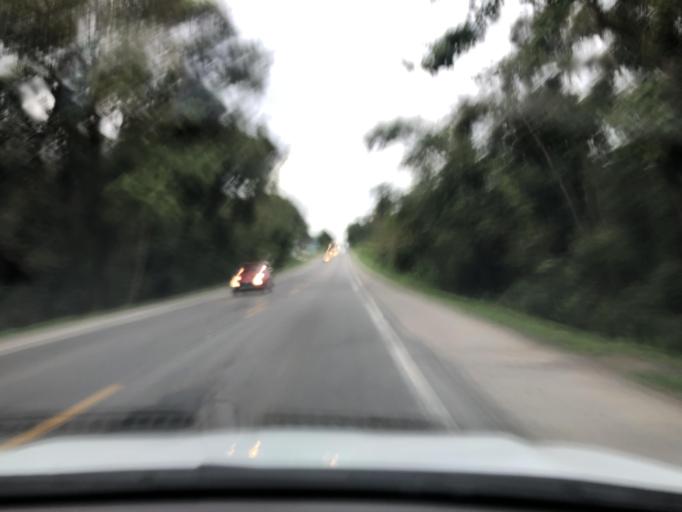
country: BR
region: Santa Catarina
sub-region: Sao Francisco Do Sul
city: Sao Francisco do Sul
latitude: -26.3142
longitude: -48.6449
